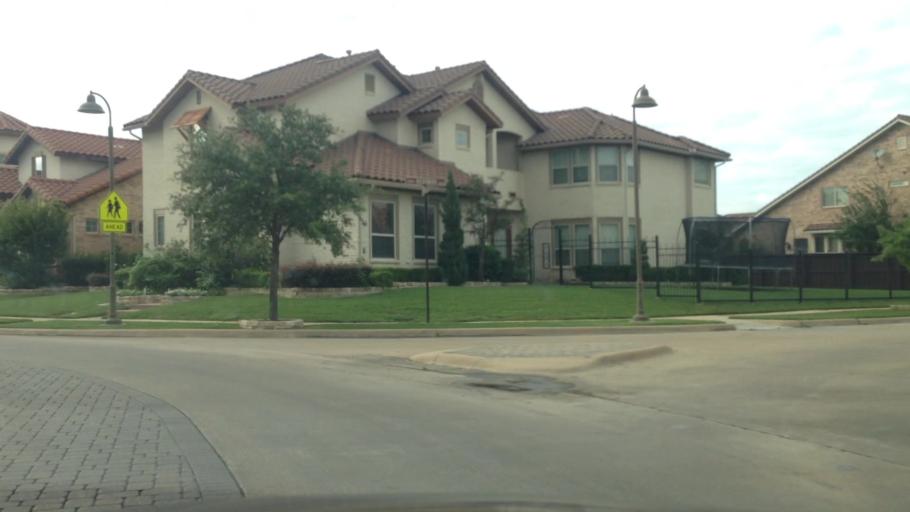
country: US
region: Texas
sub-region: Dallas County
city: Farmers Branch
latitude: 32.9033
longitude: -96.9343
